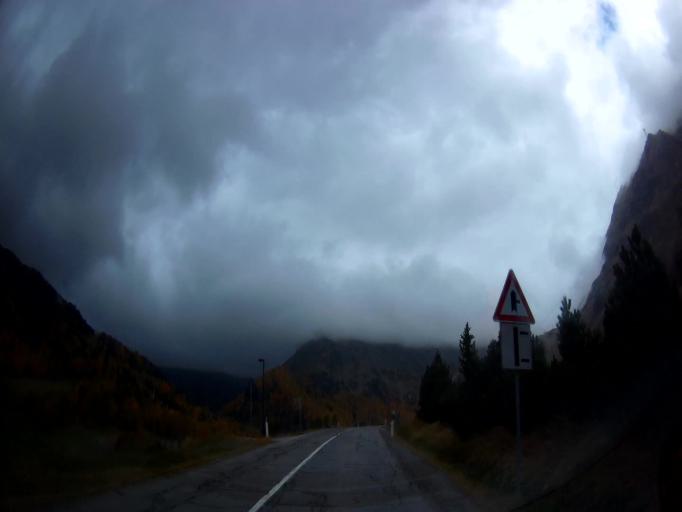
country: IT
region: Trentino-Alto Adige
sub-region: Bolzano
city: Silandro
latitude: 46.7528
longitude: 10.7852
